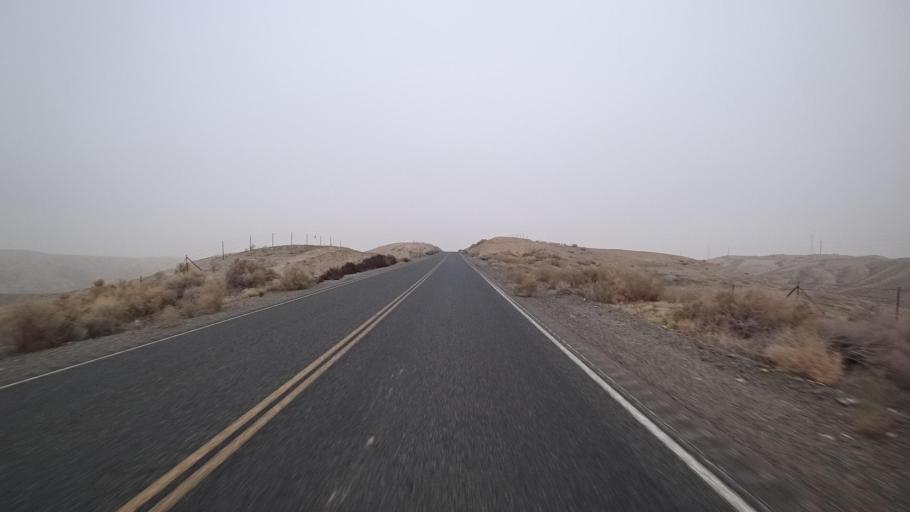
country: US
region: California
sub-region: Kern County
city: Buttonwillow
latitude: 35.3116
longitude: -119.4677
